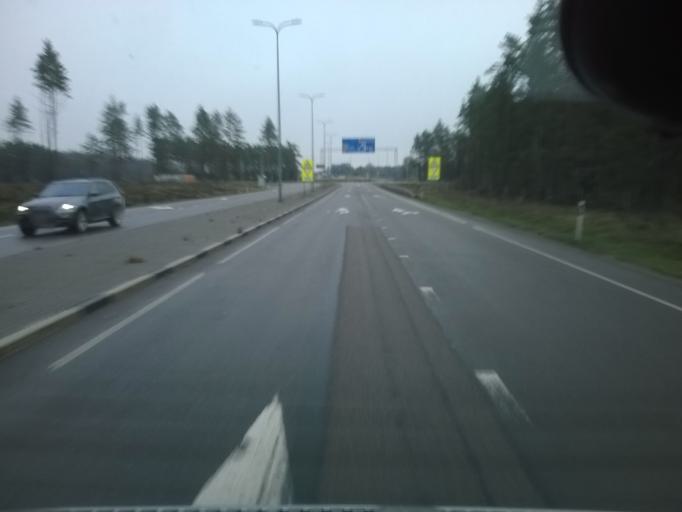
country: EE
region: Harju
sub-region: Kiili vald
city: Kiili
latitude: 59.3175
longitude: 24.7595
